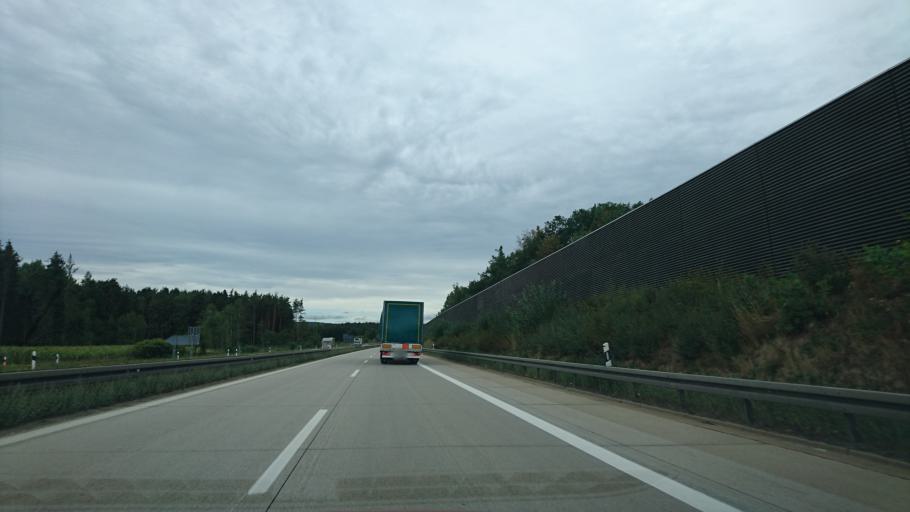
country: DE
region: Bavaria
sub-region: Upper Palatinate
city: Wernberg-Koblitz
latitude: 49.5355
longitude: 12.1371
